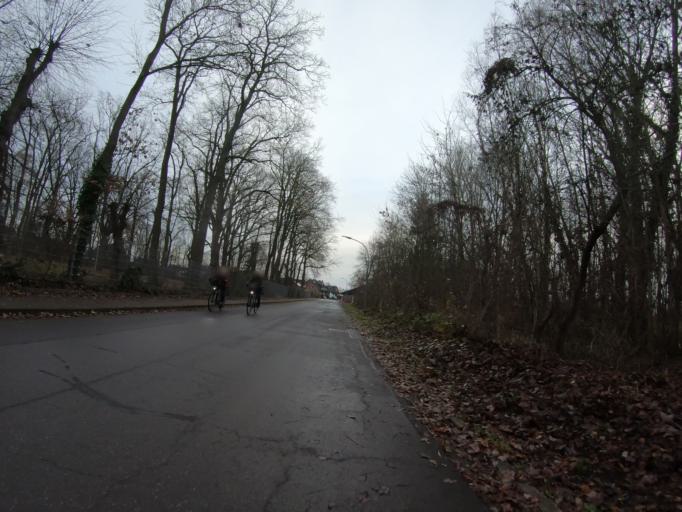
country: DE
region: Lower Saxony
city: Isenbuttel
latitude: 52.4291
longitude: 10.5794
